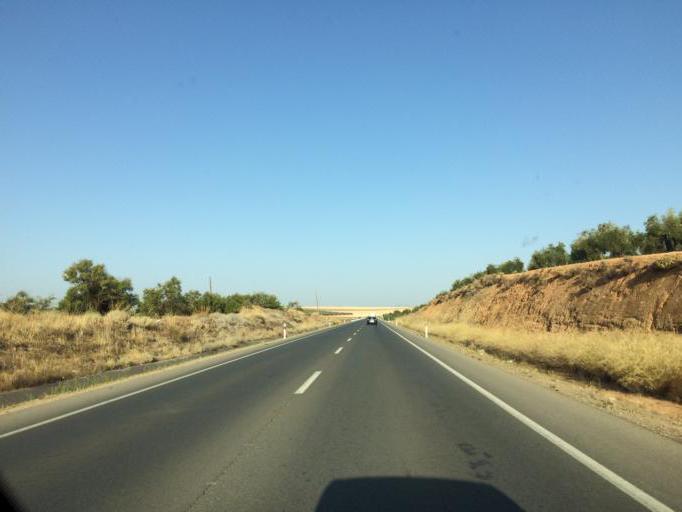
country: ES
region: Andalusia
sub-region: Provincia de Malaga
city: Campillos
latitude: 37.0517
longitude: -4.7913
